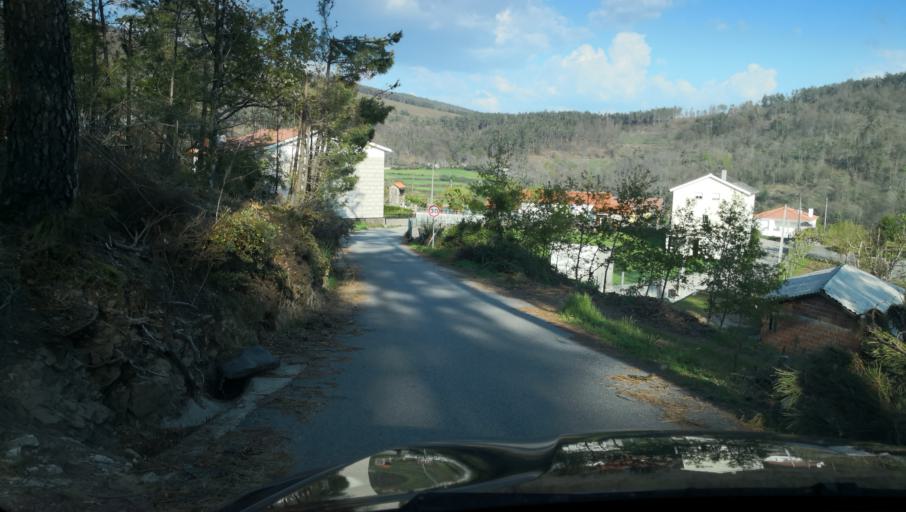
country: PT
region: Vila Real
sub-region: Vila Real
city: Vila Real
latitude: 41.3144
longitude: -7.8626
